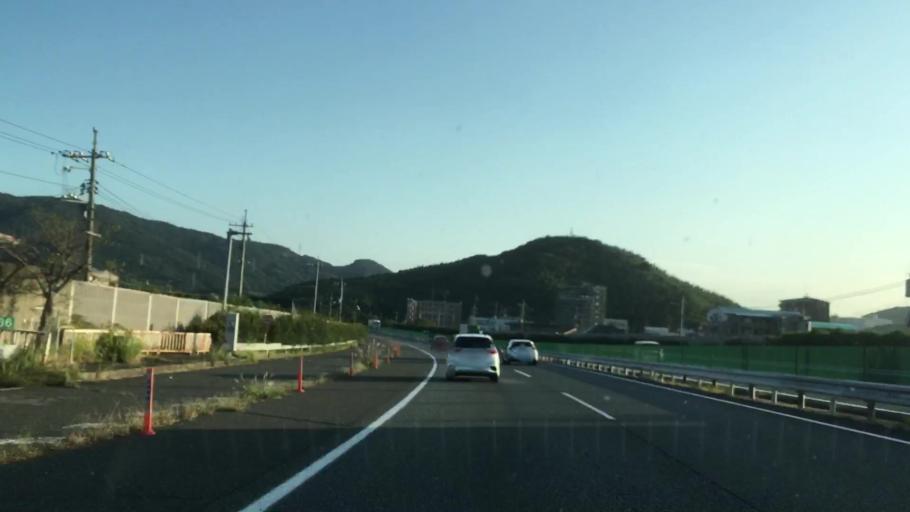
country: JP
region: Yamaguchi
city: Shimonoseki
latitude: 34.0126
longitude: 130.9554
